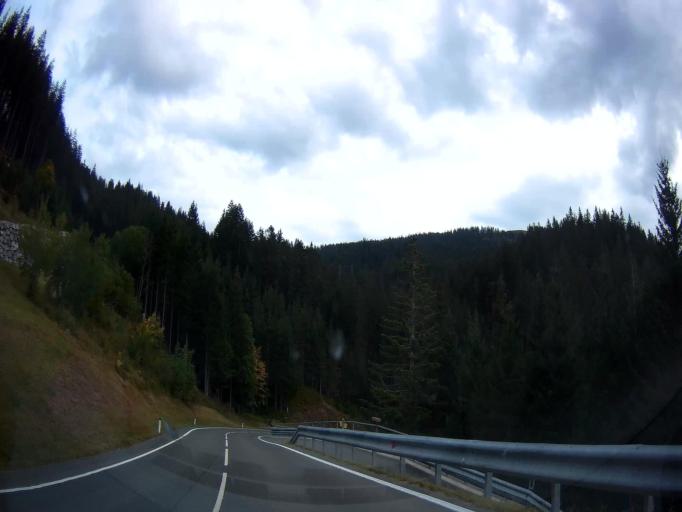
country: AT
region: Salzburg
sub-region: Politischer Bezirk Zell am See
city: Dienten am Hochkonig
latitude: 47.4052
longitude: 12.9915
